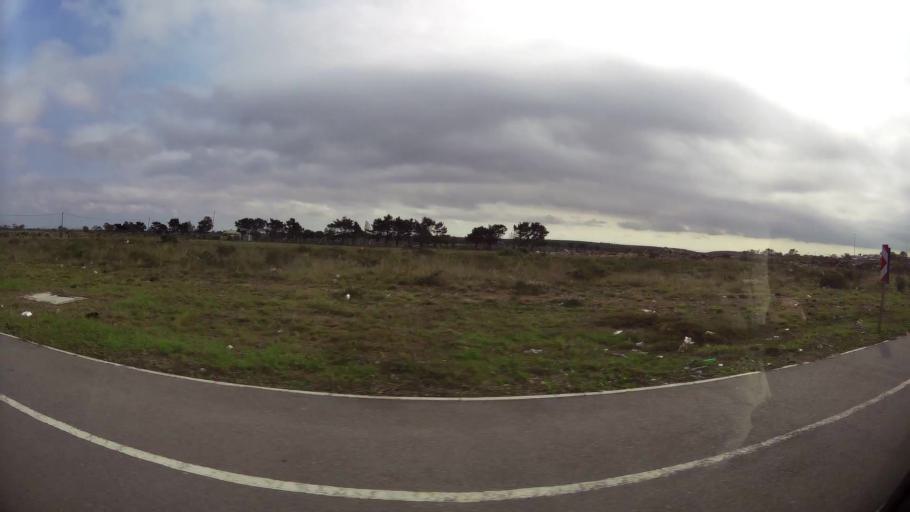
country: ZA
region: Eastern Cape
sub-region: Nelson Mandela Bay Metropolitan Municipality
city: Port Elizabeth
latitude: -33.9180
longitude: 25.5305
